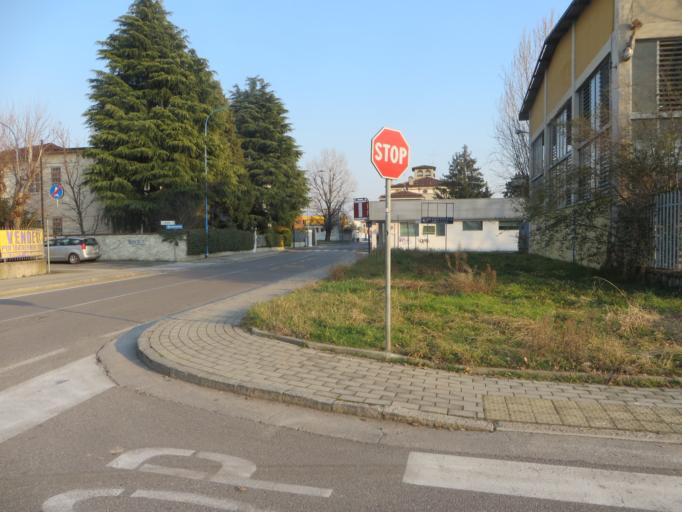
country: IT
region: Lombardy
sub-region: Provincia di Brescia
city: Brescia
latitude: 45.5254
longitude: 10.1953
